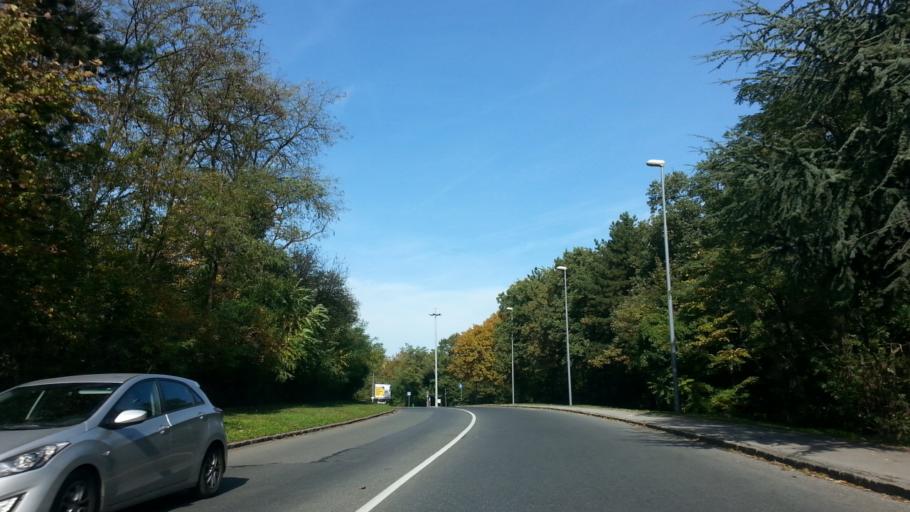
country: RS
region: Central Serbia
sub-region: Belgrade
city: Rakovica
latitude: 44.7549
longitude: 20.4373
